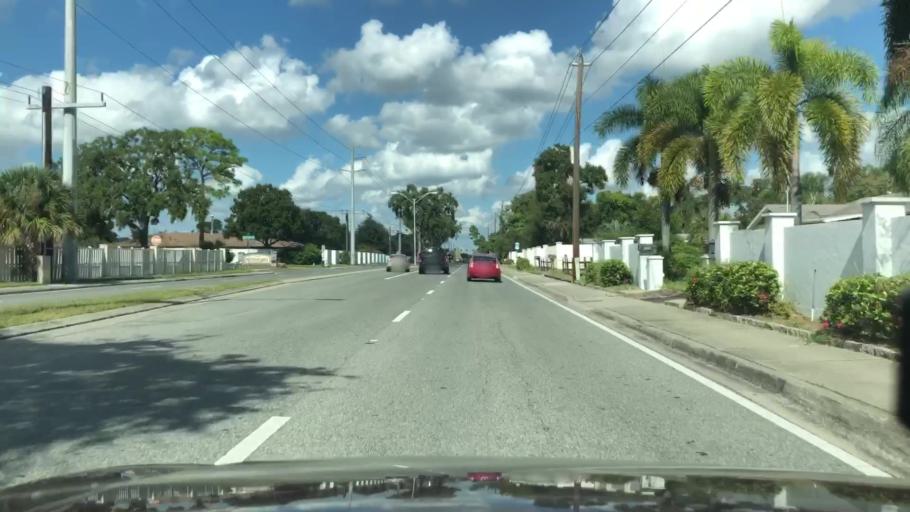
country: US
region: Florida
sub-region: Sarasota County
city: South Gate Ridge
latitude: 27.2650
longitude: -82.4975
